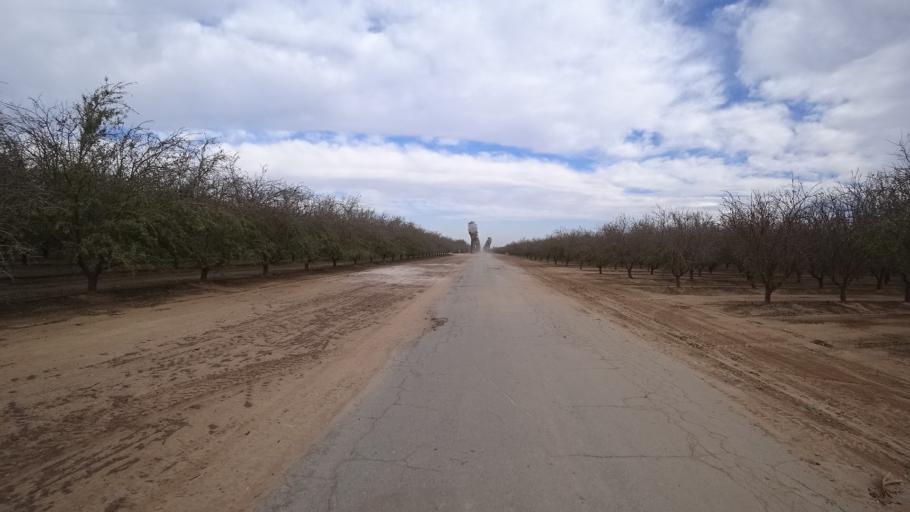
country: US
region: California
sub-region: Kern County
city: Rosedale
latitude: 35.4257
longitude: -119.1721
